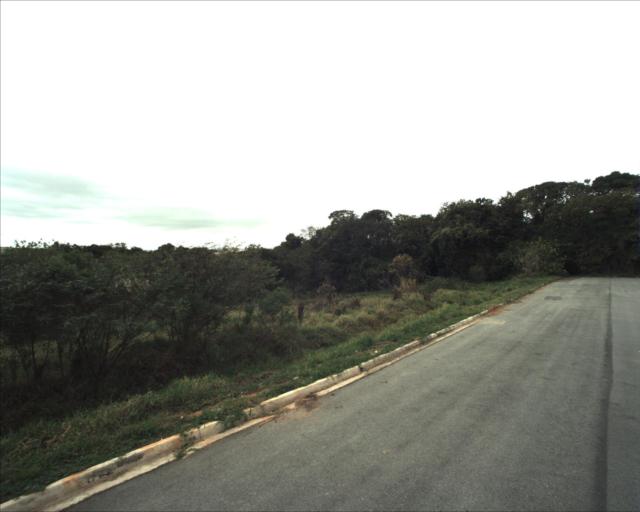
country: BR
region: Sao Paulo
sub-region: Sorocaba
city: Sorocaba
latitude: -23.4434
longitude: -47.5018
